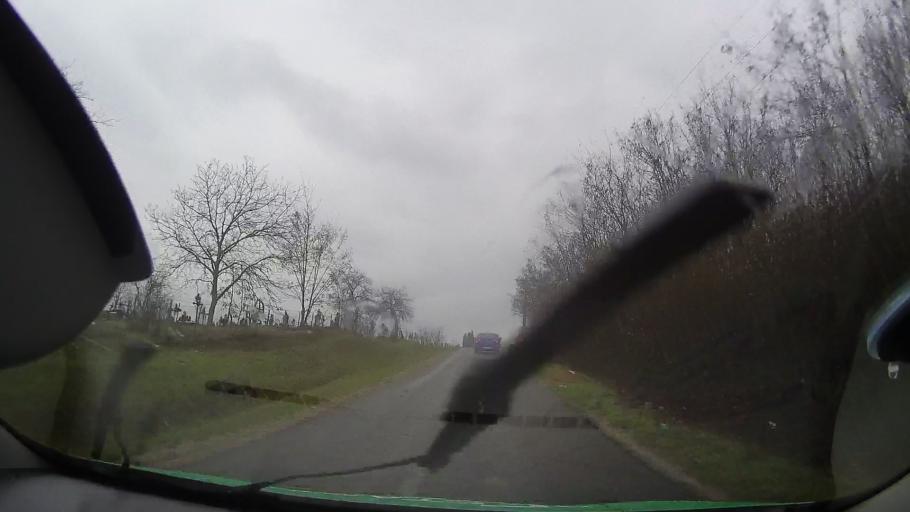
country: RO
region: Bihor
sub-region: Comuna Holod
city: Vintere
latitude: 46.7596
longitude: 22.1473
